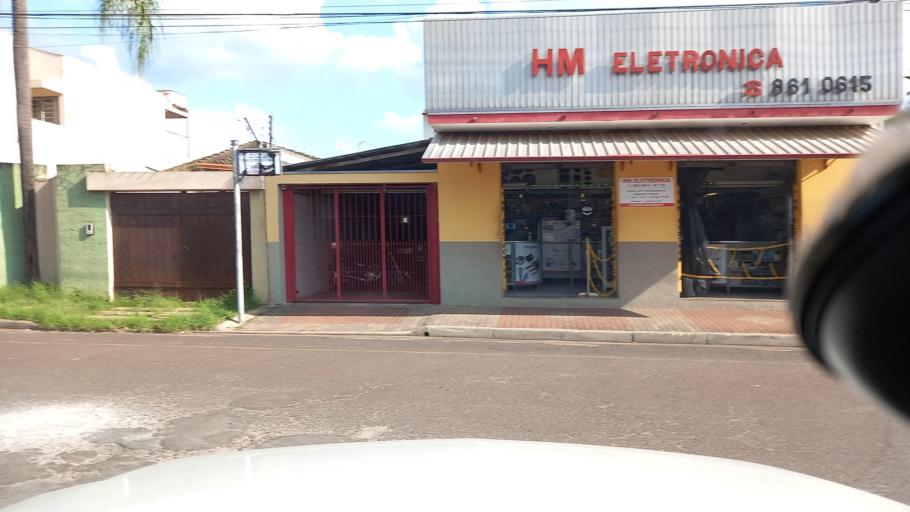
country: BR
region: Sao Paulo
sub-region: Moji-Guacu
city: Mogi-Gaucu
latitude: -22.3511
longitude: -46.9478
